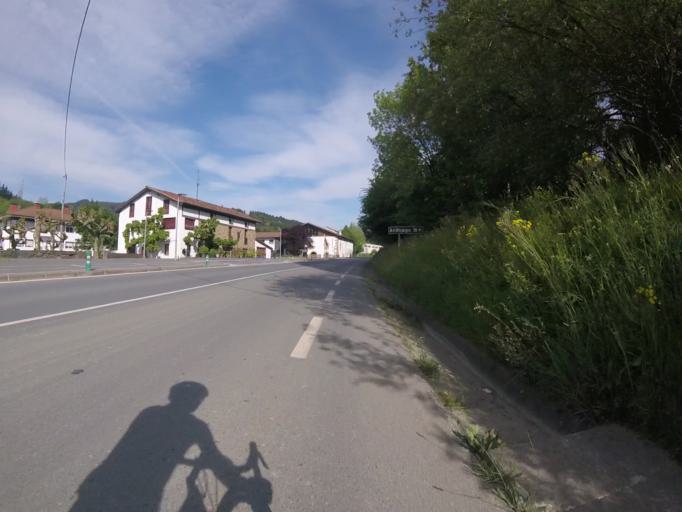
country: ES
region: Basque Country
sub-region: Provincia de Guipuzcoa
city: Gabiria
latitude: 43.0687
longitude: -2.2846
